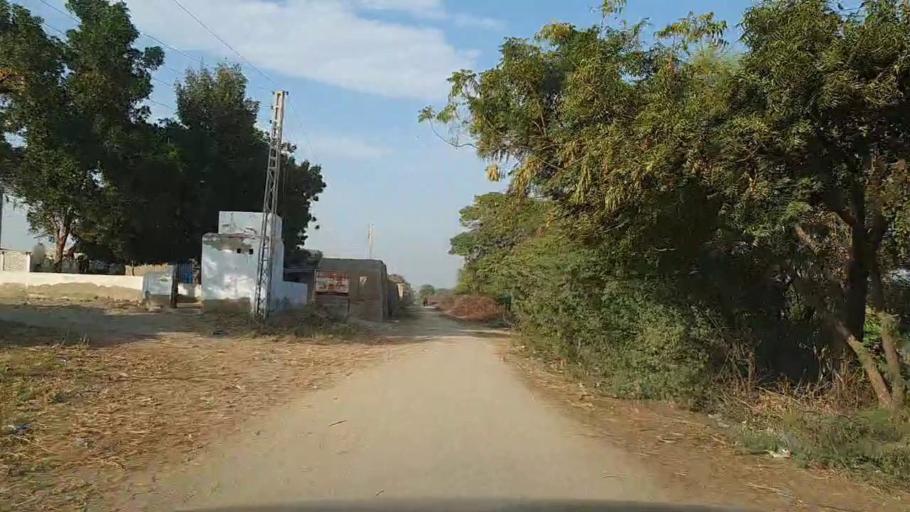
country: PK
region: Sindh
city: Daur
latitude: 26.4159
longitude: 68.4335
